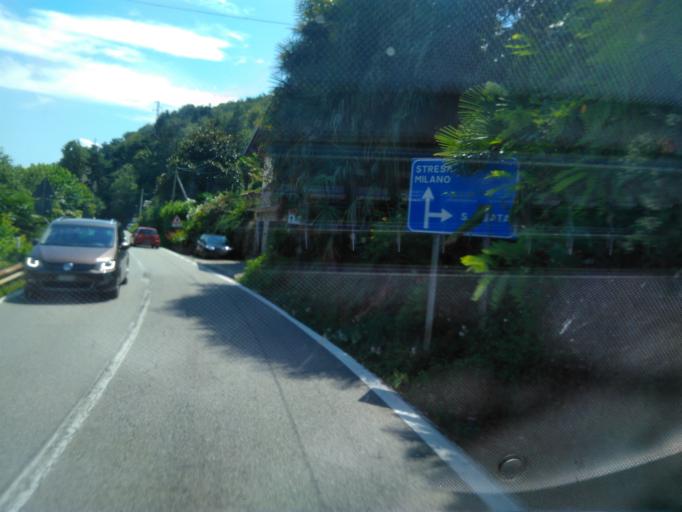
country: IT
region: Piedmont
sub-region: Provincia Verbano-Cusio-Ossola
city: Cannobio
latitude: 46.0802
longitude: 8.6927
